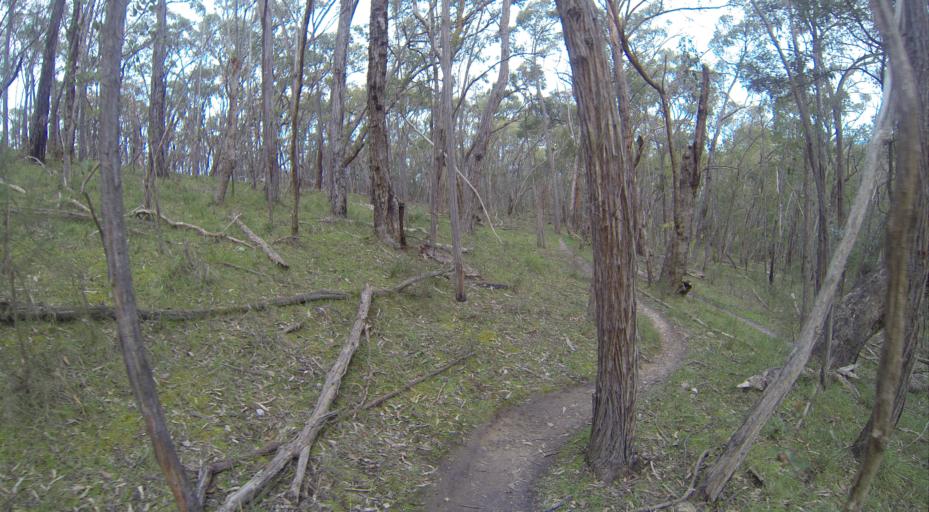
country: AU
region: Victoria
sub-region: Nillumbik
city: Saint Andrews
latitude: -37.6414
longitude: 145.2929
